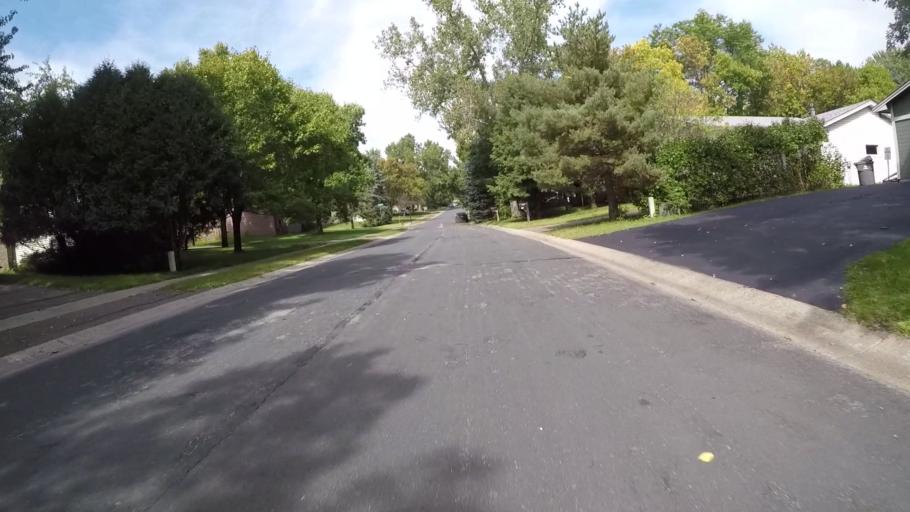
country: US
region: Minnesota
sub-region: Hennepin County
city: Eden Prairie
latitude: 44.8710
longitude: -93.4454
